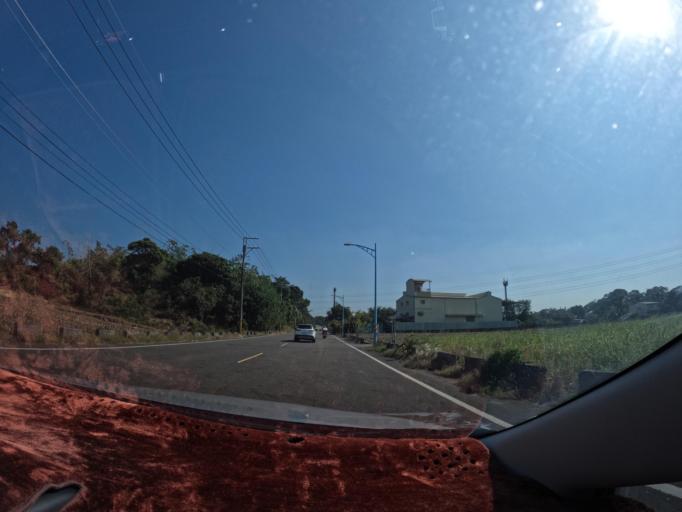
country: TW
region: Taiwan
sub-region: Tainan
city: Tainan
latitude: 23.0384
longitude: 120.3343
